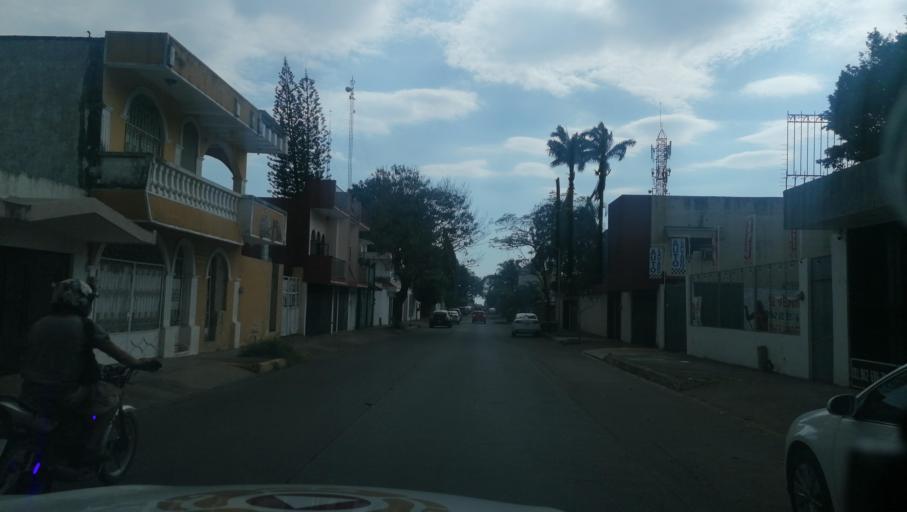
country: MX
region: Chiapas
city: Tapachula
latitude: 14.9151
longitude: -92.2538
